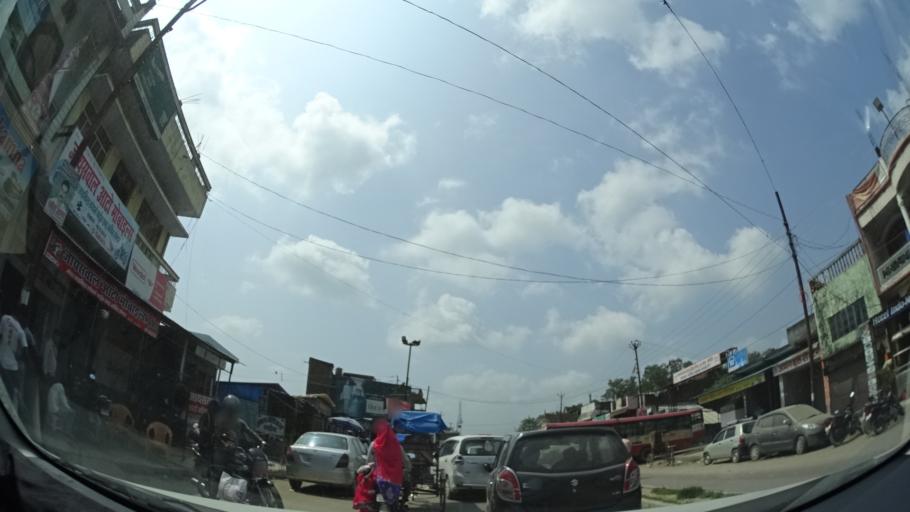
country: NP
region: Western Region
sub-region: Lumbini Zone
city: Bhairahawa
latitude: 27.4725
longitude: 83.4672
